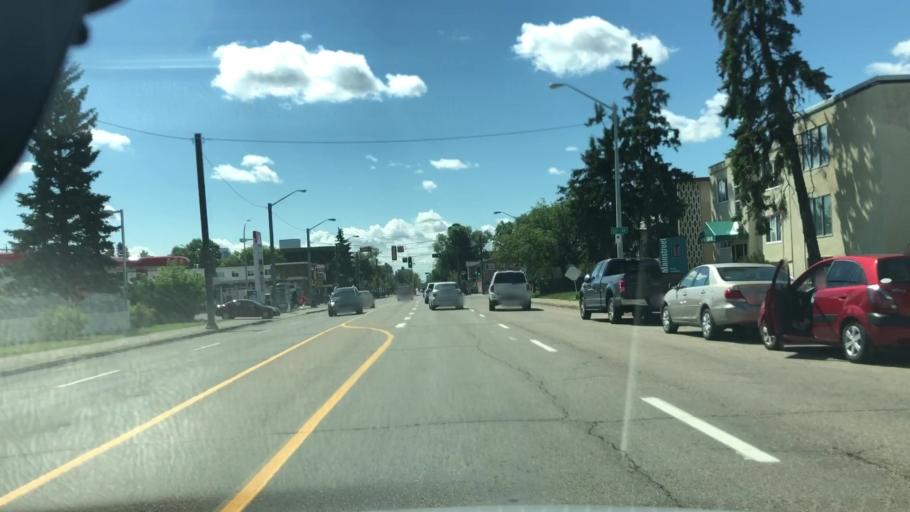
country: CA
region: Alberta
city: Edmonton
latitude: 53.5599
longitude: -113.5360
